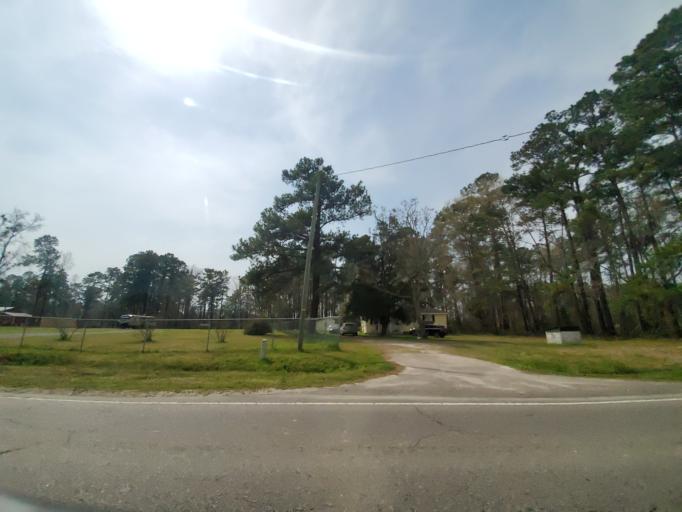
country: US
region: South Carolina
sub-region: Dorchester County
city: Ridgeville
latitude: 32.9882
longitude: -80.3068
